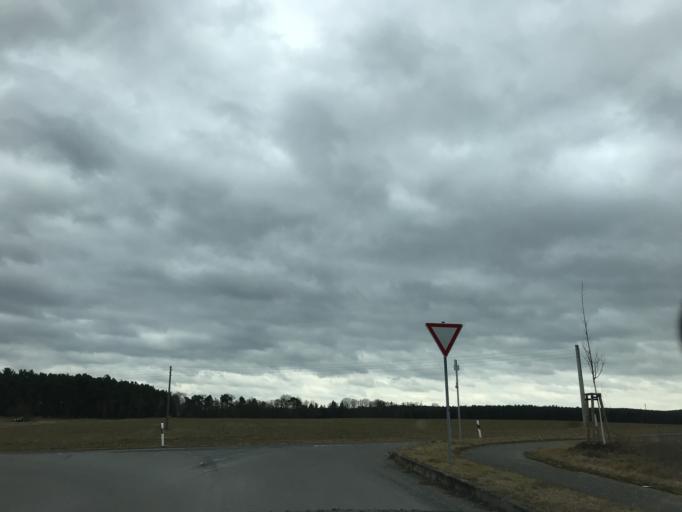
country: DE
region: Brandenburg
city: Crinitz
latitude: 51.7553
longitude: 13.8113
